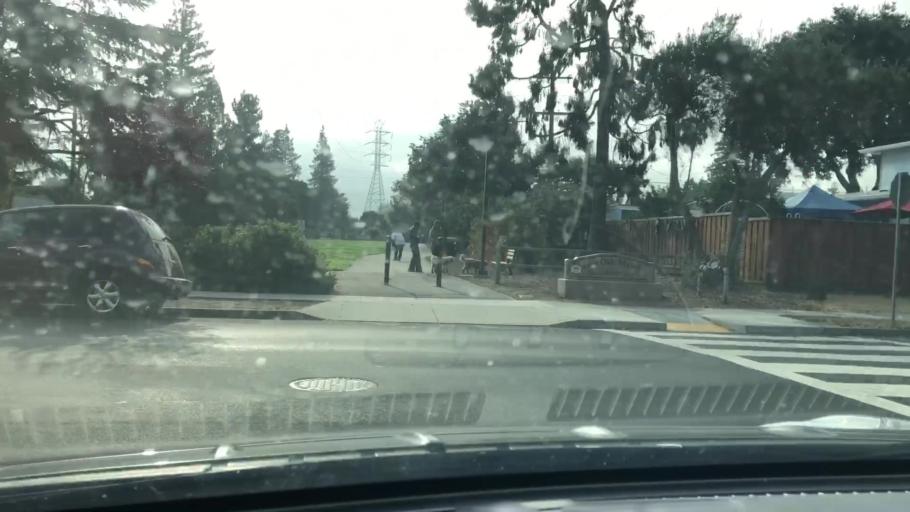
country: US
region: California
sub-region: Santa Clara County
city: Los Gatos
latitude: 37.2459
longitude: -121.9569
